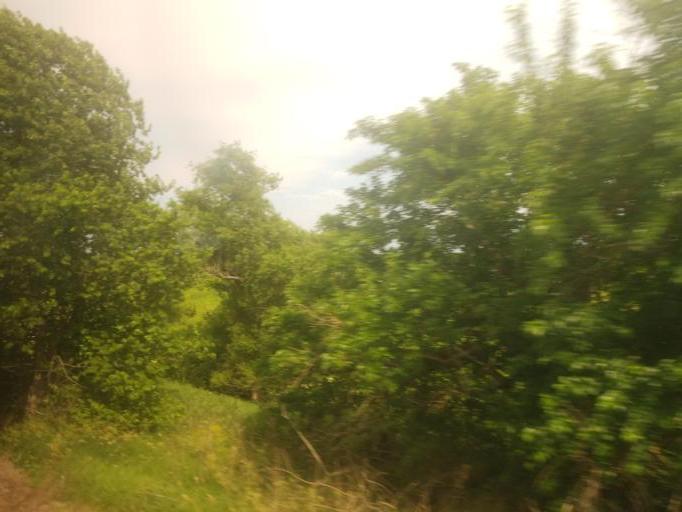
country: US
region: Illinois
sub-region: Henry County
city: Galva
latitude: 41.1469
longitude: -90.0873
